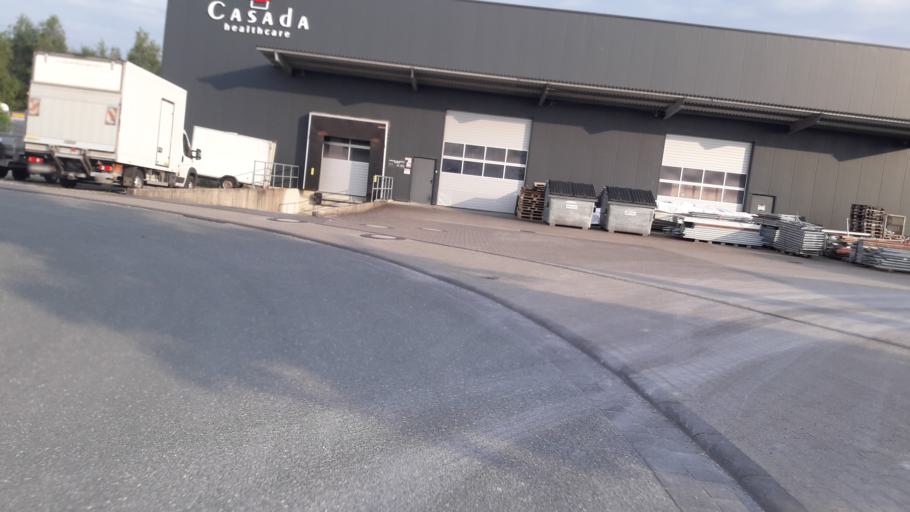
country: DE
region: North Rhine-Westphalia
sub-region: Regierungsbezirk Detmold
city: Hovelhof
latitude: 51.7895
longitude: 8.6976
